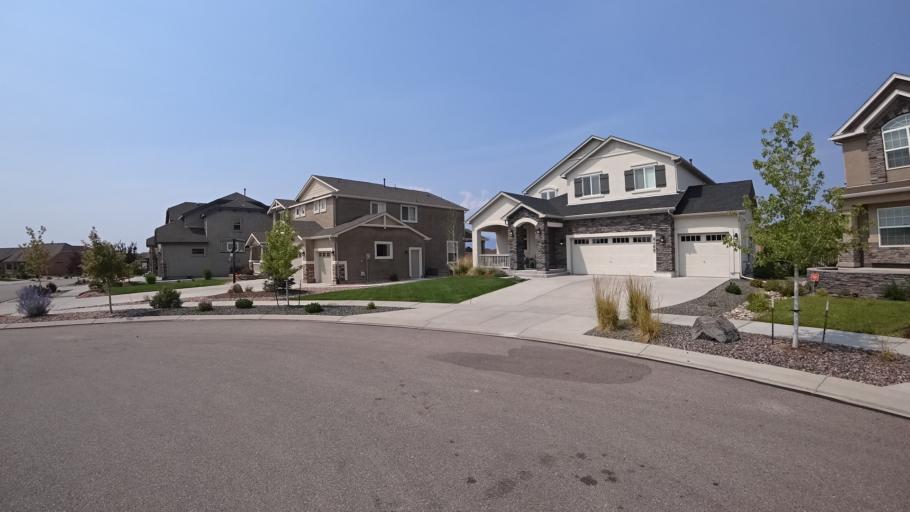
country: US
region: Colorado
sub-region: El Paso County
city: Black Forest
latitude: 38.9648
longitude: -104.7147
